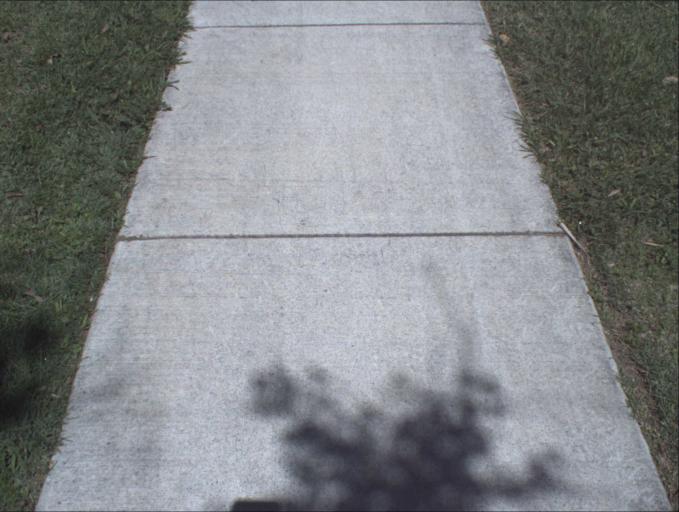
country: AU
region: Queensland
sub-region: Logan
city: Waterford West
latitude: -27.7012
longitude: 153.1615
